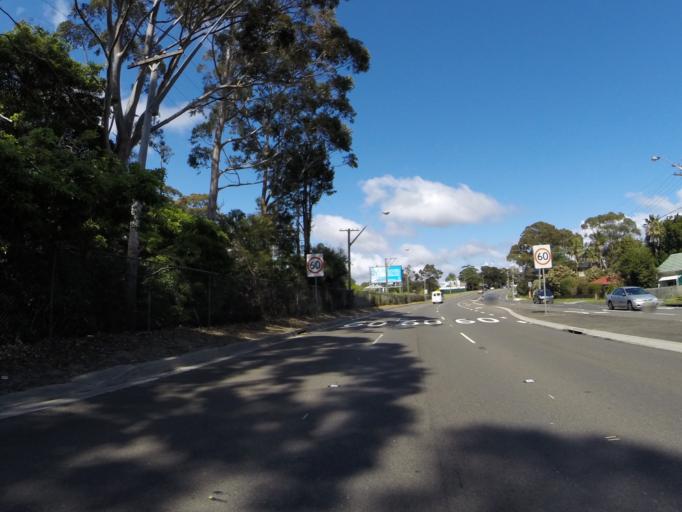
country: AU
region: New South Wales
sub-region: Sutherland Shire
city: Heathcote
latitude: -34.0842
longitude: 151.0110
